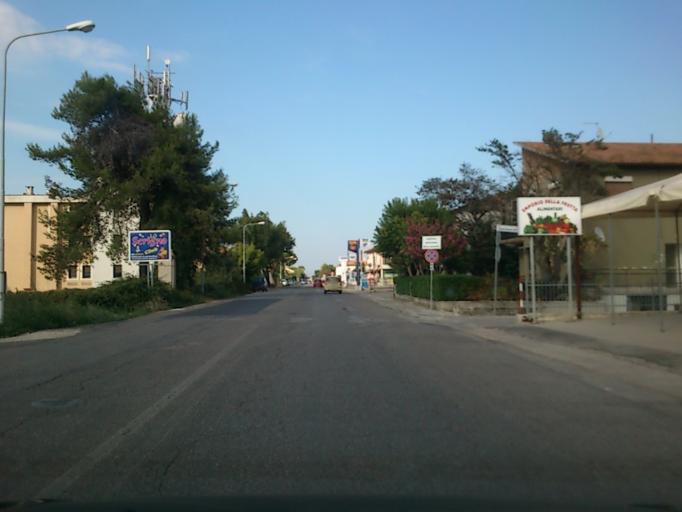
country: IT
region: The Marches
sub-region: Provincia di Pesaro e Urbino
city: Centinarola
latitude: 43.8296
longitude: 12.9980
